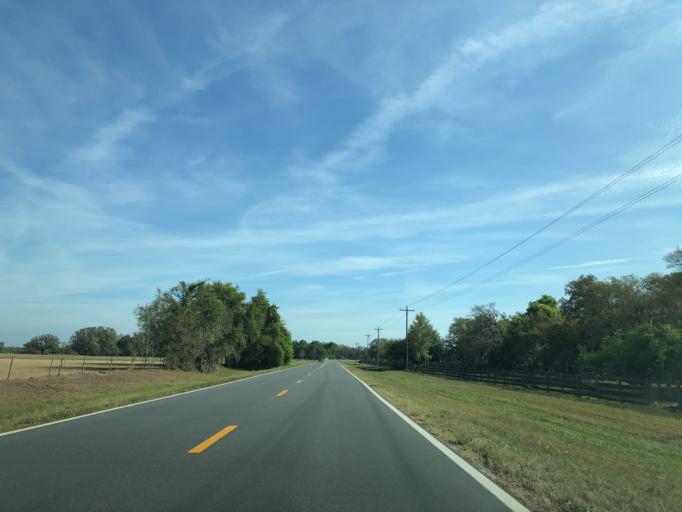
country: US
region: Florida
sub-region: Lake County
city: Astatula
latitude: 28.7190
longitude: -81.7059
